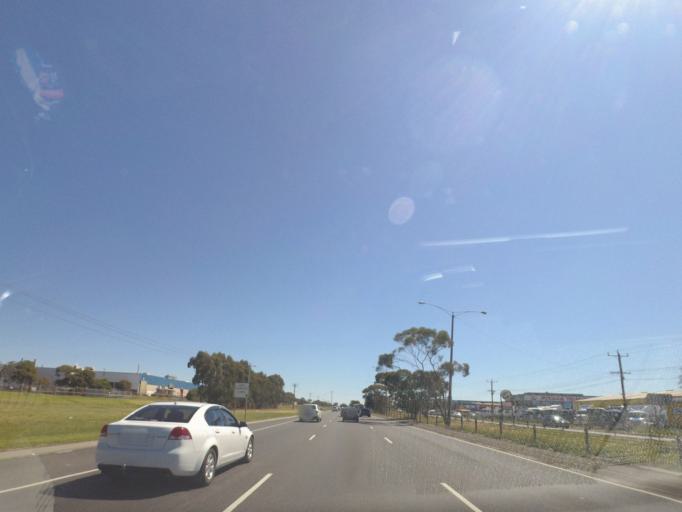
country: AU
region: Victoria
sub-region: Hume
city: Campbellfield
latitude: -37.6656
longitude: 144.9546
